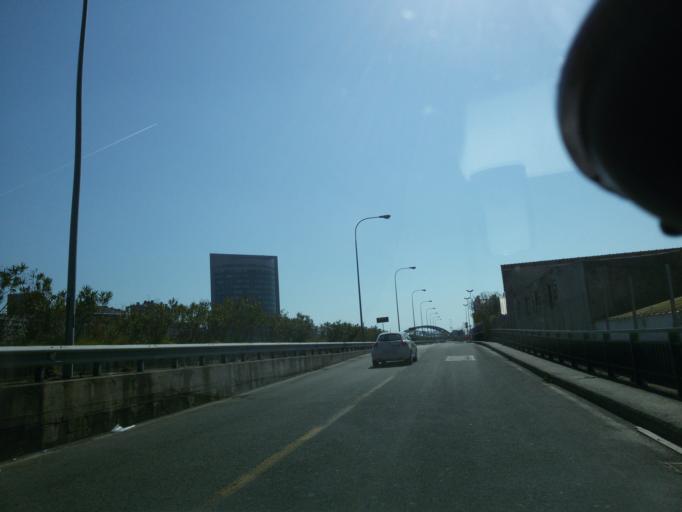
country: IT
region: Liguria
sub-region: Provincia di Genova
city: San Teodoro
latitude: 44.4184
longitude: 8.8817
